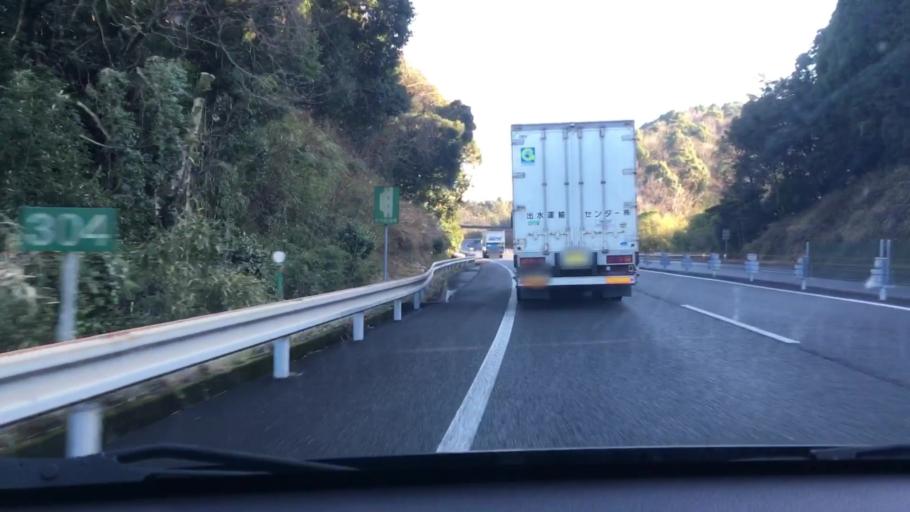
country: JP
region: Kagoshima
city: Kajiki
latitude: 31.8346
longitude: 130.6906
